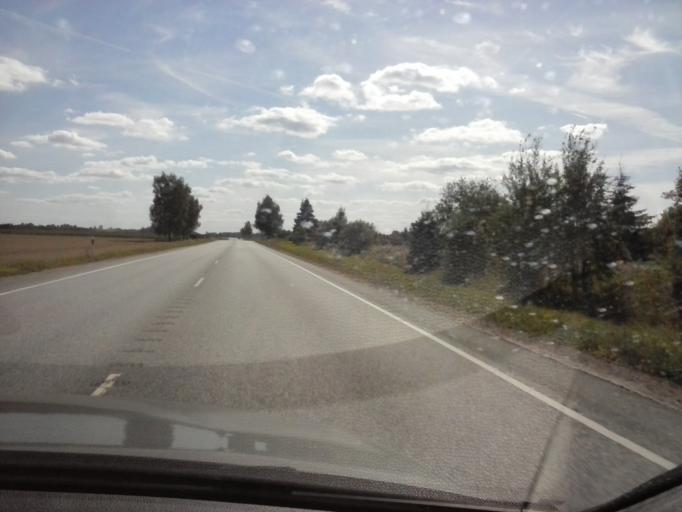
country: EE
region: Jaervamaa
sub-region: Paide linn
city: Paide
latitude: 58.7915
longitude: 25.7570
